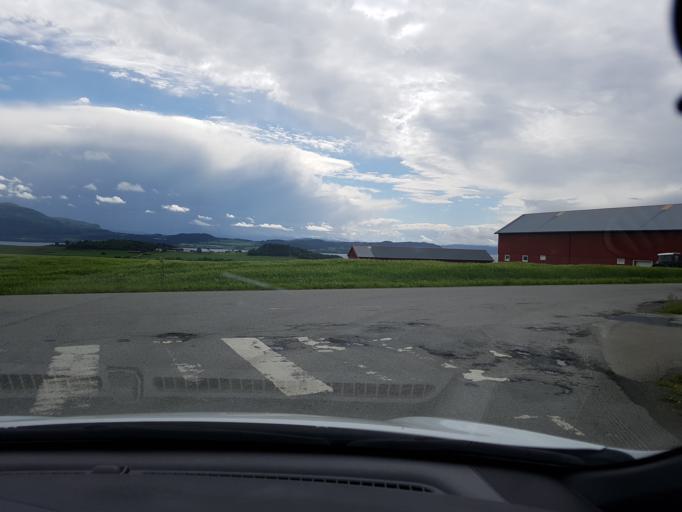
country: NO
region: Nord-Trondelag
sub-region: Frosta
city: Frosta
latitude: 63.5871
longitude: 10.7408
